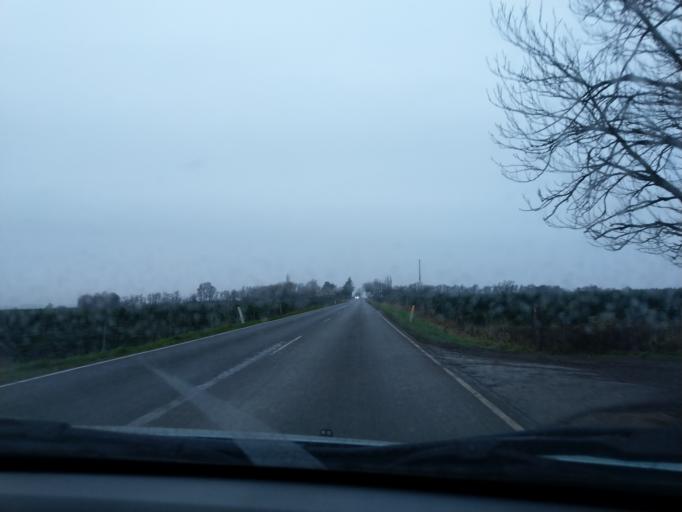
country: DK
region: Zealand
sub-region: Vordingborg Kommune
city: Orslev
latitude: 55.1198
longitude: 11.9769
